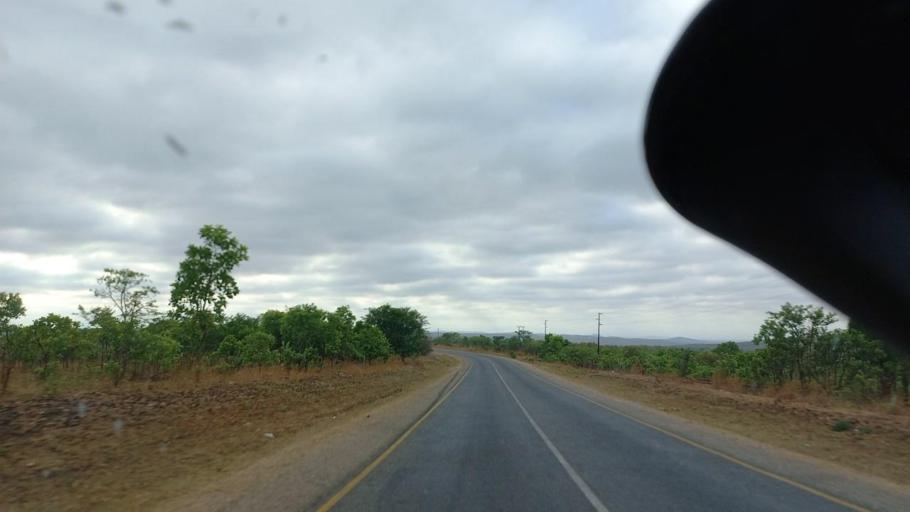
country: ZM
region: Lusaka
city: Chongwe
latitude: -15.2757
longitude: 28.7700
